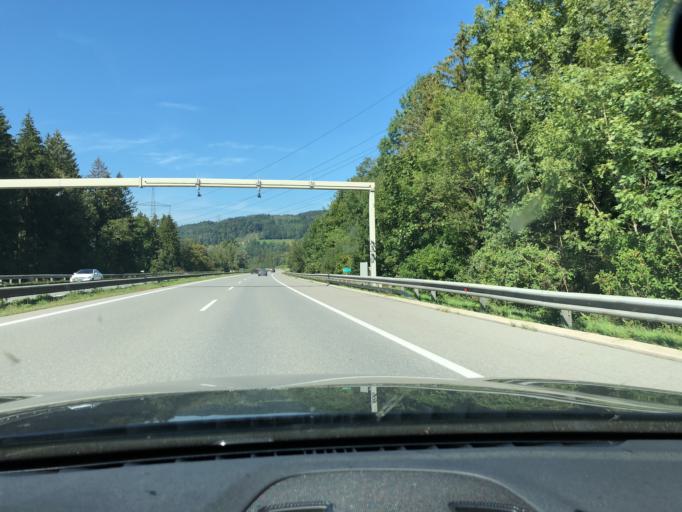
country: AT
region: Vorarlberg
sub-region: Politischer Bezirk Feldkirch
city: Satteins
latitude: 47.2148
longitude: 9.6597
